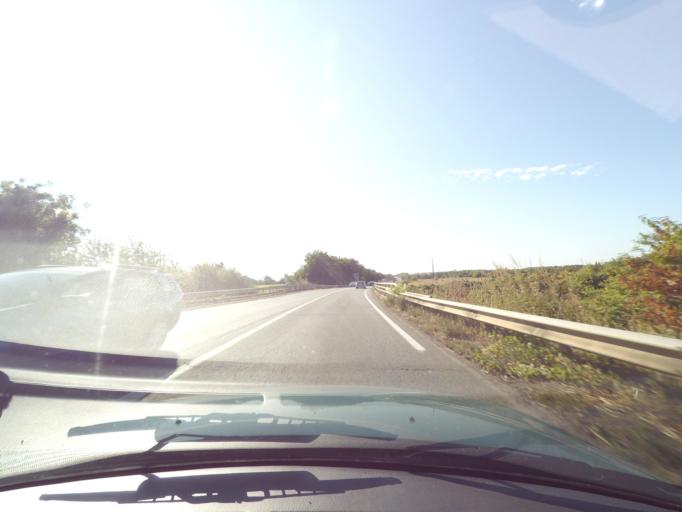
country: FR
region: Poitou-Charentes
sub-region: Departement de la Vienne
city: Migne-Auxances
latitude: 46.6326
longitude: 0.2913
